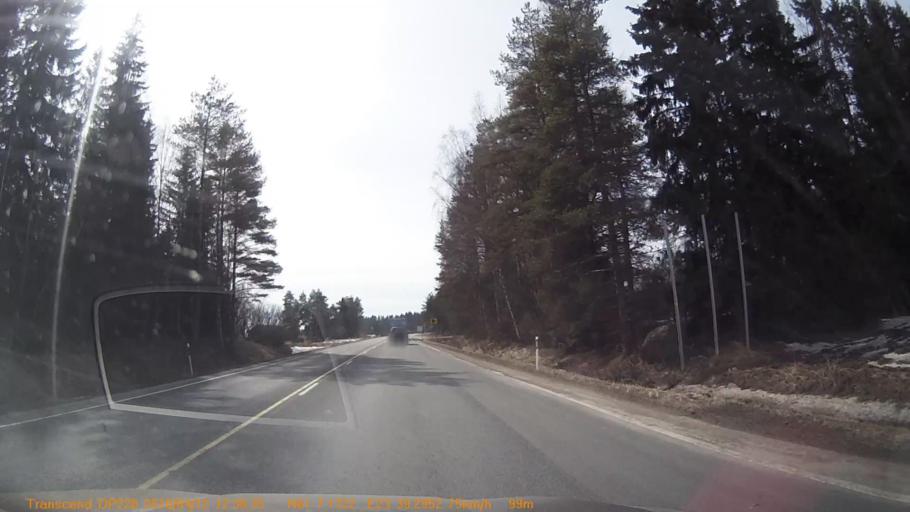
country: FI
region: Pirkanmaa
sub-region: Etelae-Pirkanmaa
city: Kylmaekoski
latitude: 61.1196
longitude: 23.6551
